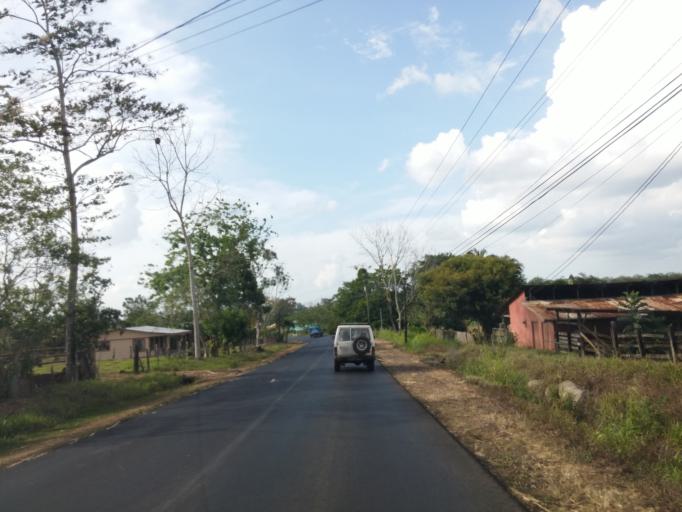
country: CR
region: Alajuela
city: Quesada
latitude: 10.4236
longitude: -84.4678
